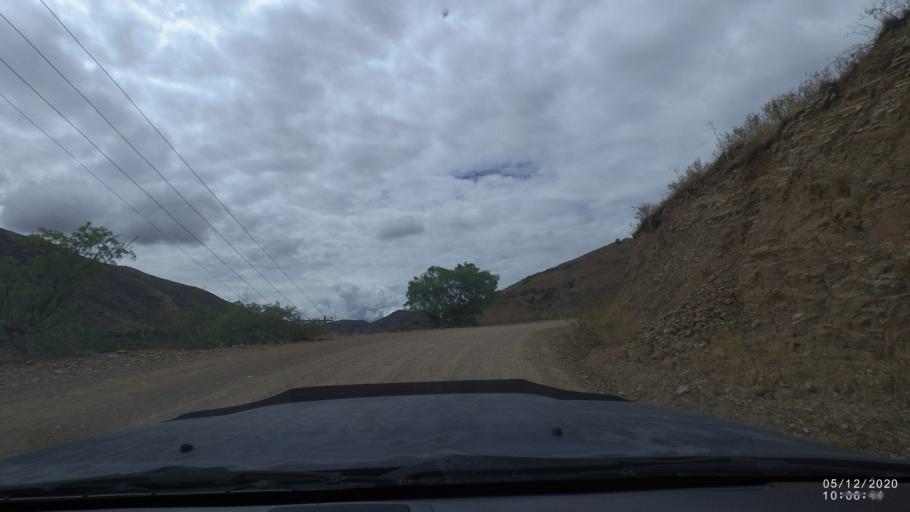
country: BO
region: Cochabamba
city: Sipe Sipe
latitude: -17.4776
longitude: -66.2839
